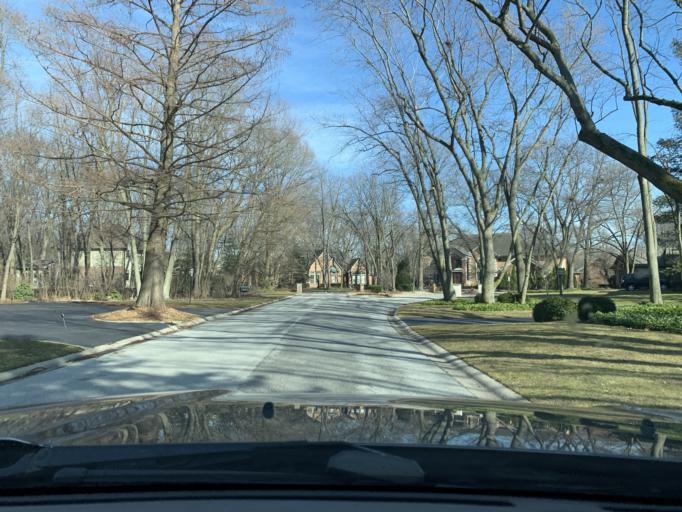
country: US
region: Indiana
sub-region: Lake County
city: Dyer
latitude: 41.5159
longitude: -87.4837
